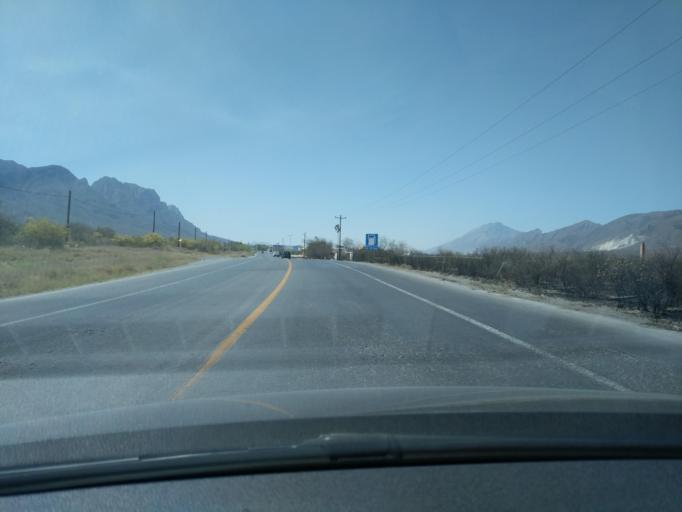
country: MX
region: Nuevo Leon
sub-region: Salinas Victoria
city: Las Torres
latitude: 25.9231
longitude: -100.3715
